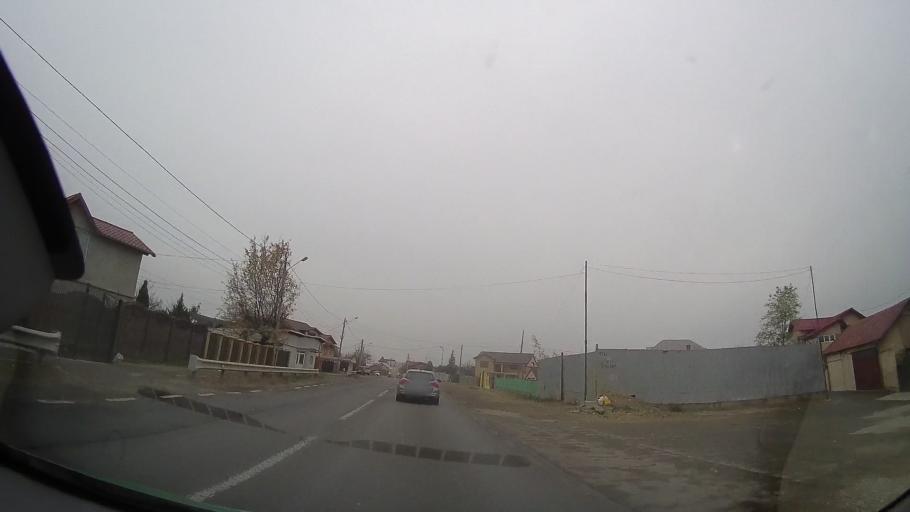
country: RO
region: Prahova
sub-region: Comuna Blejoiu
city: Ploiestiori
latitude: 44.9654
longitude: 26.0305
